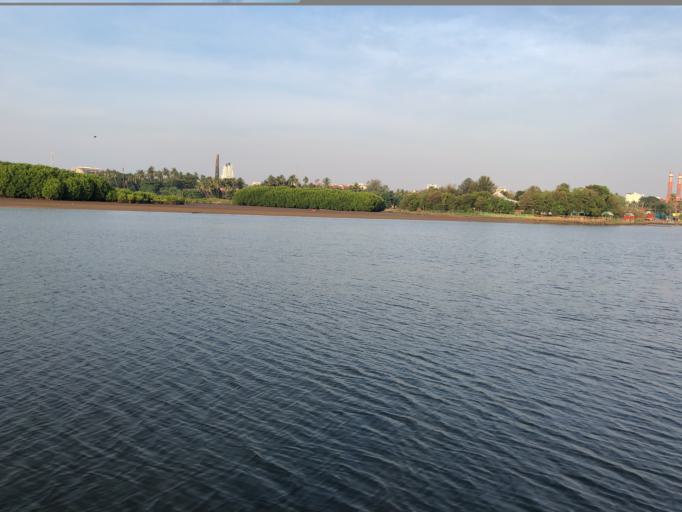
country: IN
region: Karnataka
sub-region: Dakshina Kannada
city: Mangalore
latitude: 12.8767
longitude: 74.8237
